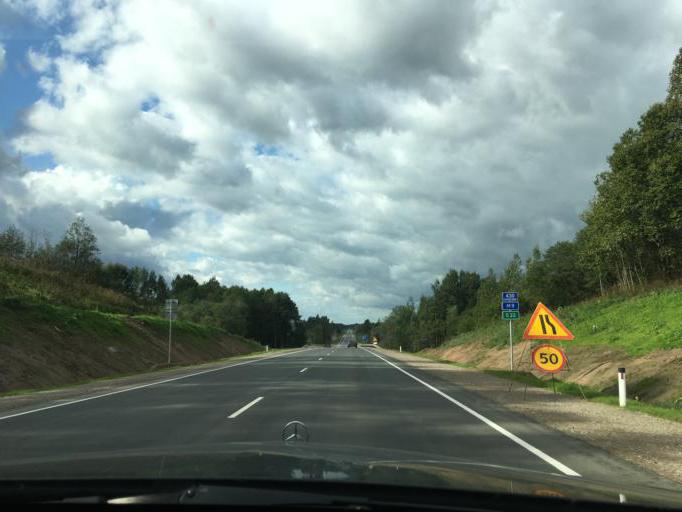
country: RU
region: Pskov
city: Velikiye Luki
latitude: 56.3035
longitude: 31.0891
